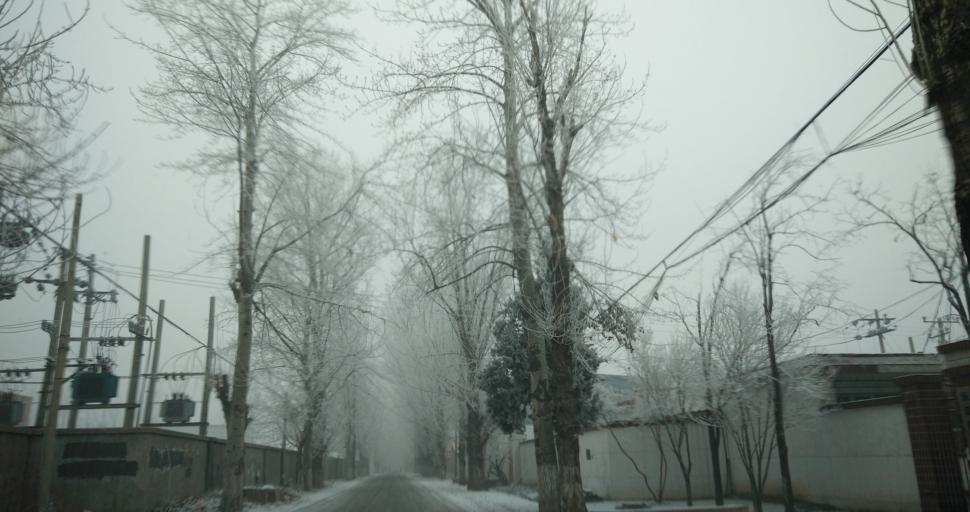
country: CN
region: Beijing
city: Yinghai
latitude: 39.7117
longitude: 116.4282
